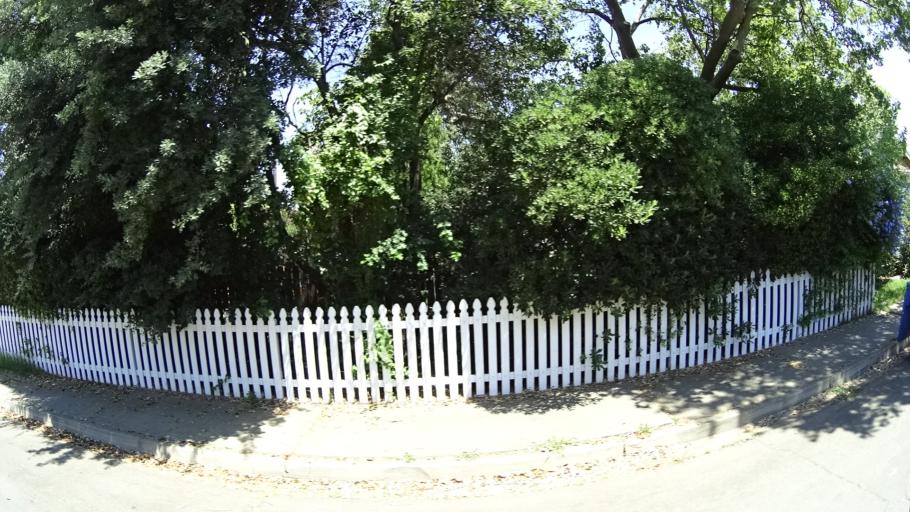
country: US
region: California
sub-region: Sacramento County
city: Sacramento
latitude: 38.5584
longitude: -121.4465
